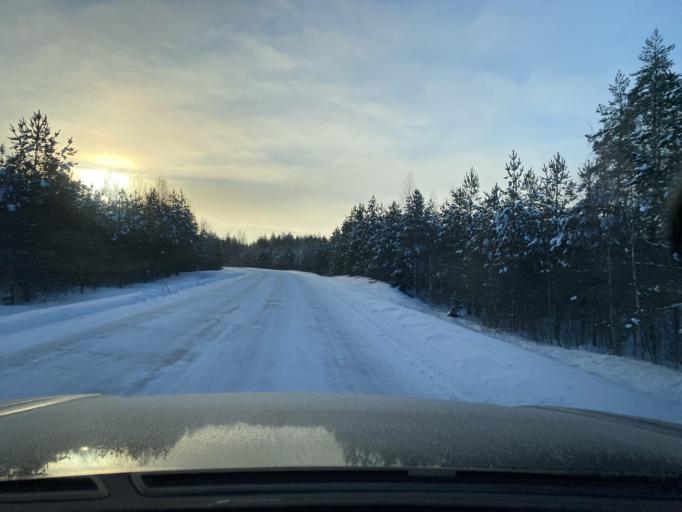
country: FI
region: Haeme
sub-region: Forssa
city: Tammela
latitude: 60.9021
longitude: 23.8826
